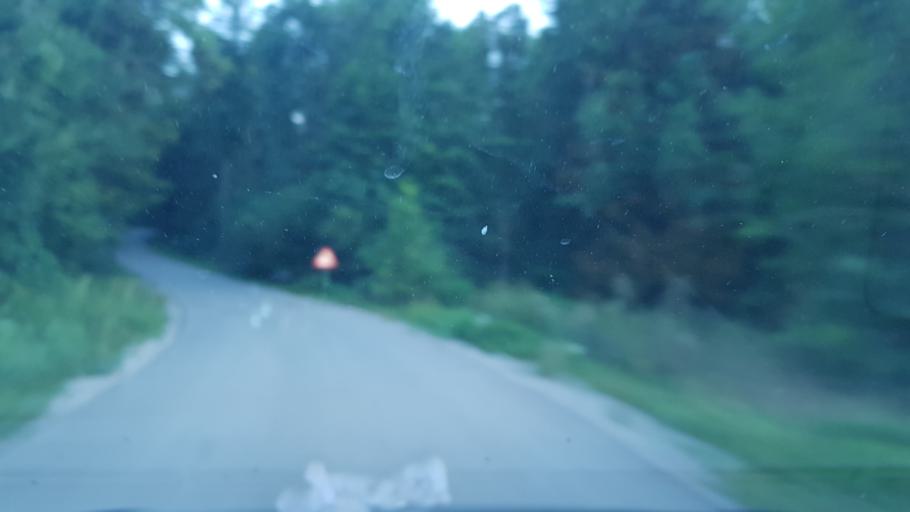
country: SI
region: Postojna
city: Postojna
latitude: 45.7482
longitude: 14.1797
